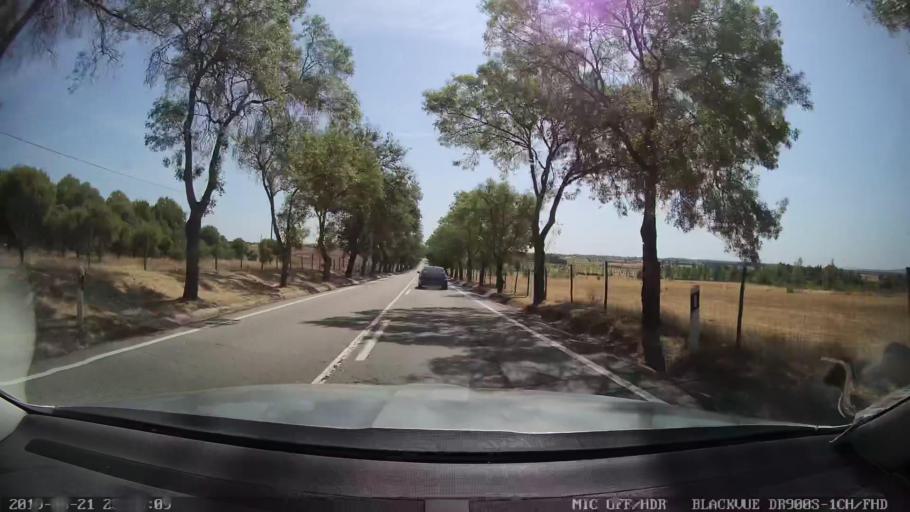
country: PT
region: Castelo Branco
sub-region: Idanha-A-Nova
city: Idanha-a-Nova
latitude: 39.8513
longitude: -7.3005
